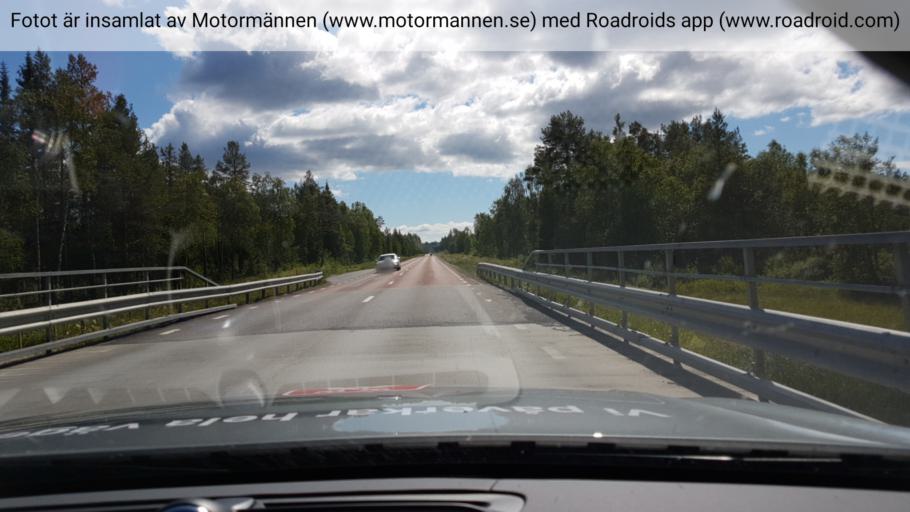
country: SE
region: Jaemtland
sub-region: Stroemsunds Kommun
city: Stroemsund
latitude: 63.7576
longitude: 15.4991
